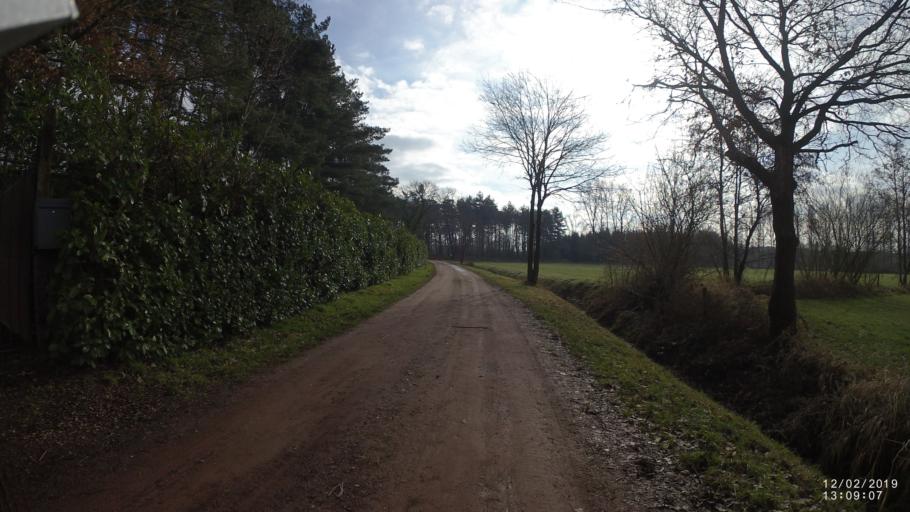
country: BE
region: Flanders
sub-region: Provincie Vlaams-Brabant
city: Scherpenheuvel-Zichem
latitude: 51.0076
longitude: 4.9221
